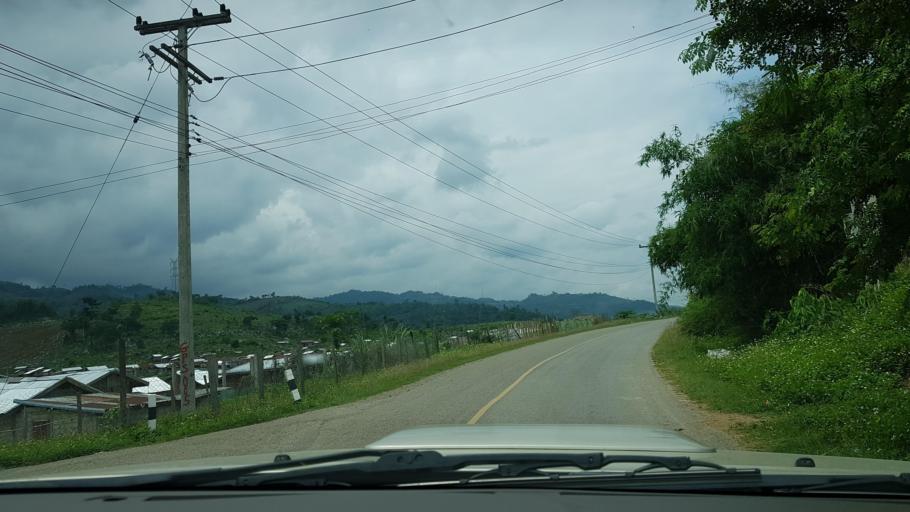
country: TH
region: Nan
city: Chaloem Phra Kiat
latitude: 19.9727
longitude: 101.2670
